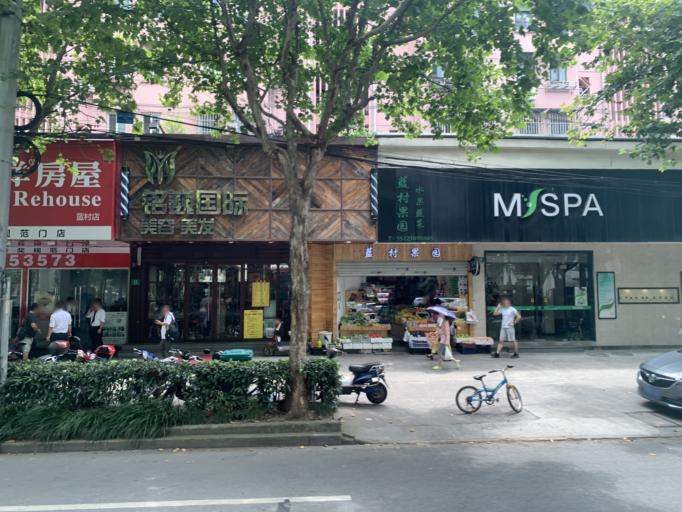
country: CN
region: Shanghai Shi
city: Huamu
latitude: 31.2136
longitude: 121.5270
